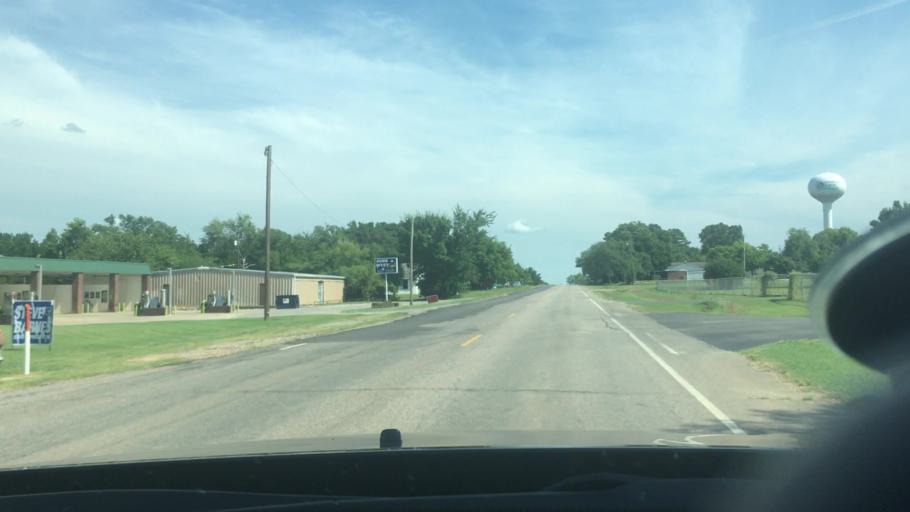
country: US
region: Oklahoma
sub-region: Seminole County
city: Seminole
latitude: 35.2392
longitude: -96.6944
